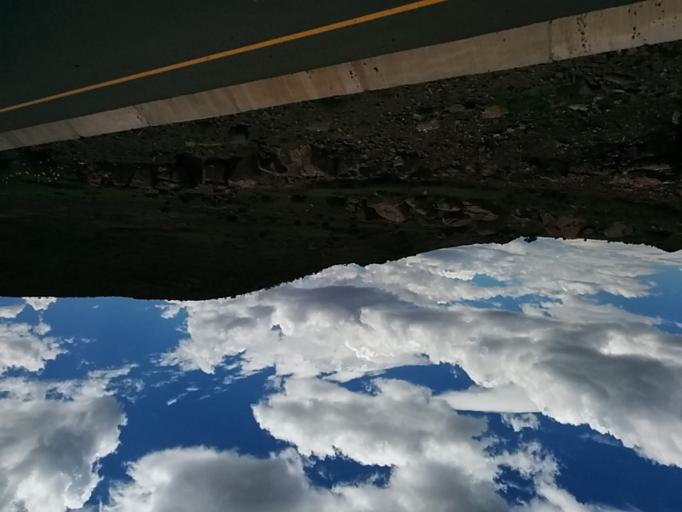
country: LS
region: Maseru
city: Nako
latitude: -29.9665
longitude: 28.1651
